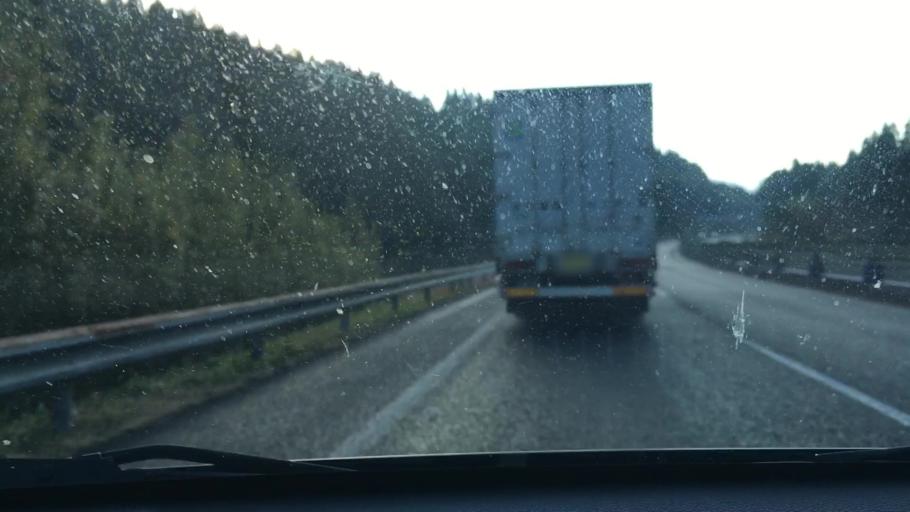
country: JP
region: Kagoshima
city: Okuchi-shinohara
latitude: 31.9478
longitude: 130.7309
